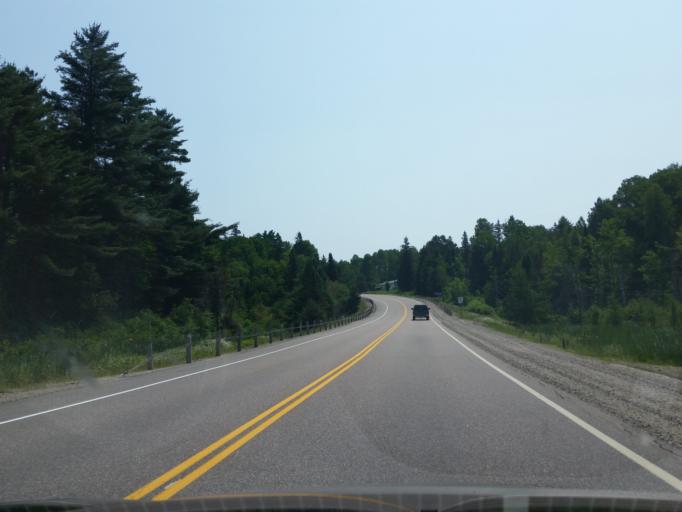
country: CA
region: Ontario
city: Deep River
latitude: 46.1724
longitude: -77.7066
